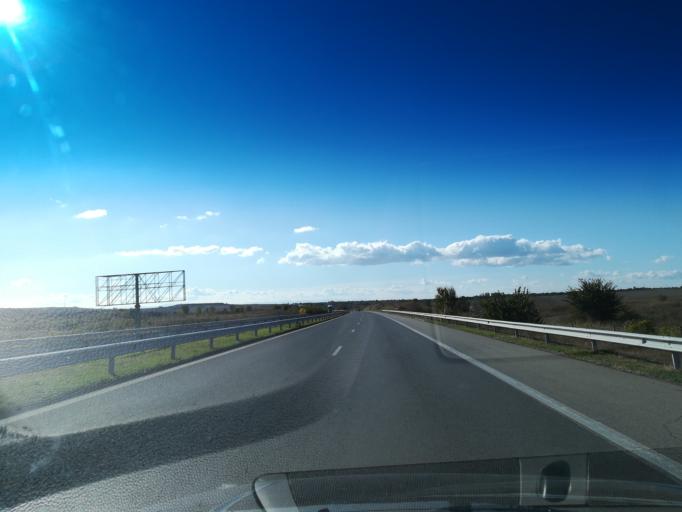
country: BG
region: Stara Zagora
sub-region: Obshtina Chirpan
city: Chirpan
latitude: 42.2441
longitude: 25.3863
